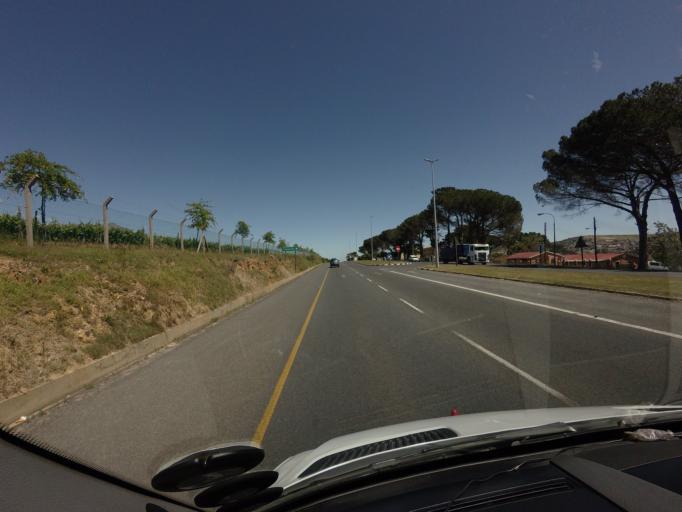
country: ZA
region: Western Cape
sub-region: Cape Winelands District Municipality
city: Stellenbosch
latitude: -33.9126
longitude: 18.8593
